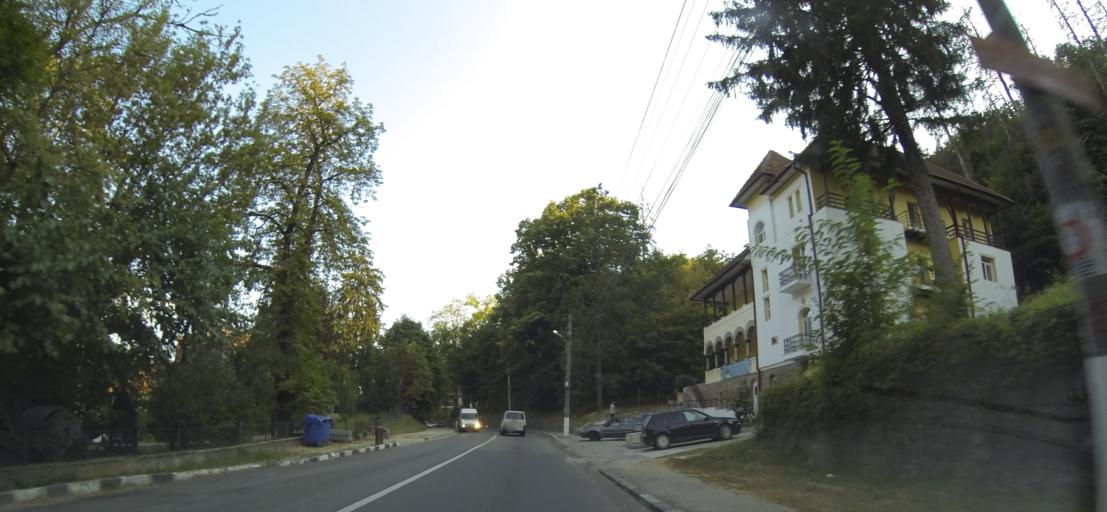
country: RO
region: Valcea
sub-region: Oras Calimanesti
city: Jiblea Veche
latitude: 45.2530
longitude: 24.3353
